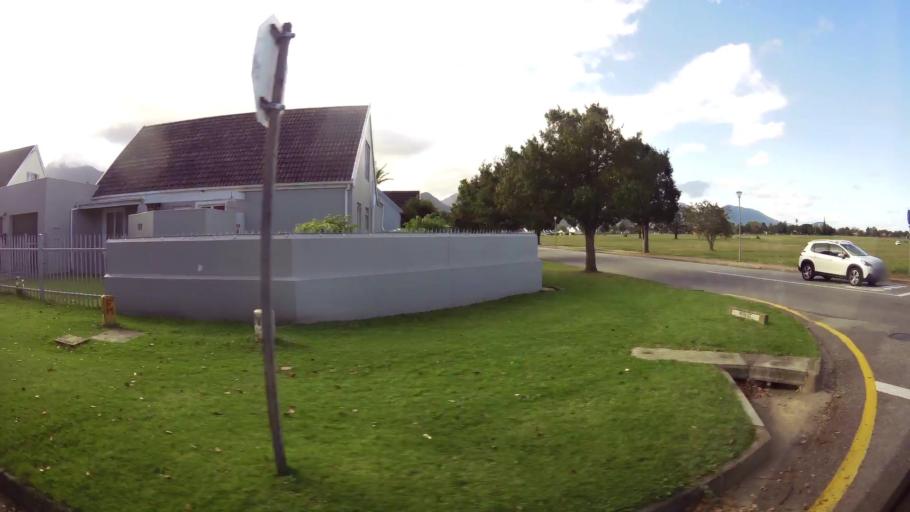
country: ZA
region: Western Cape
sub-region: Eden District Municipality
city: George
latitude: -33.9626
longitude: 22.4879
